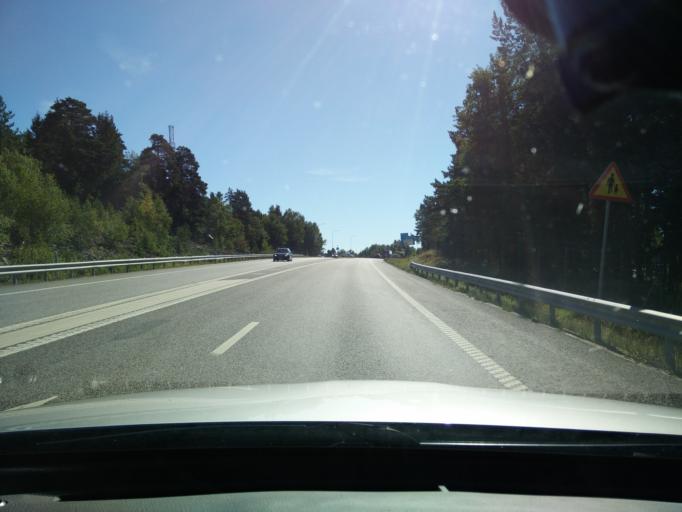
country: SE
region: Stockholm
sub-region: Osterakers Kommun
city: Akersberga
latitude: 59.4512
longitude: 18.2124
